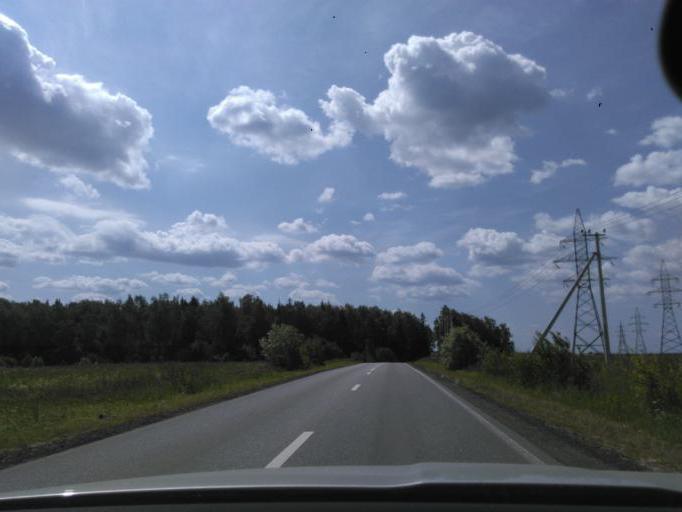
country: RU
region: Moskovskaya
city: Solnechnogorsk
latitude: 56.1430
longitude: 36.9778
